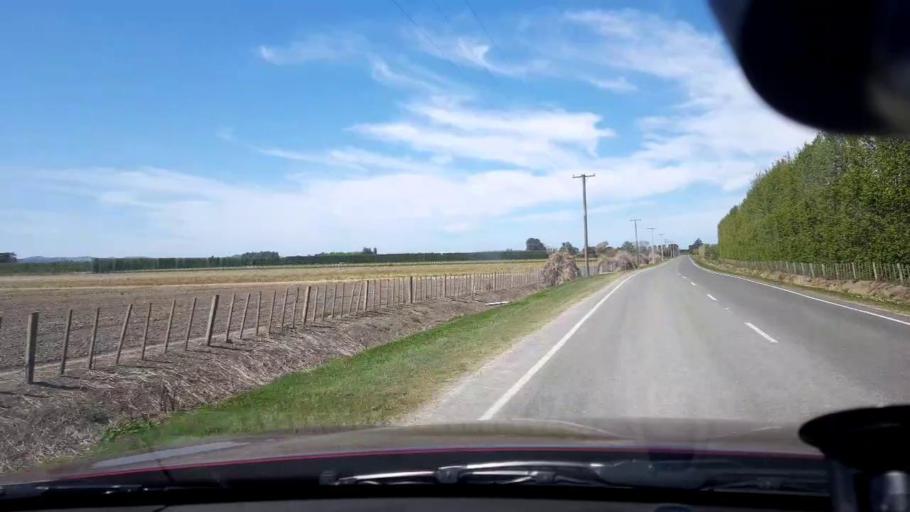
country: NZ
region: Gisborne
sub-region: Gisborne District
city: Gisborne
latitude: -38.6299
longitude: 177.9266
